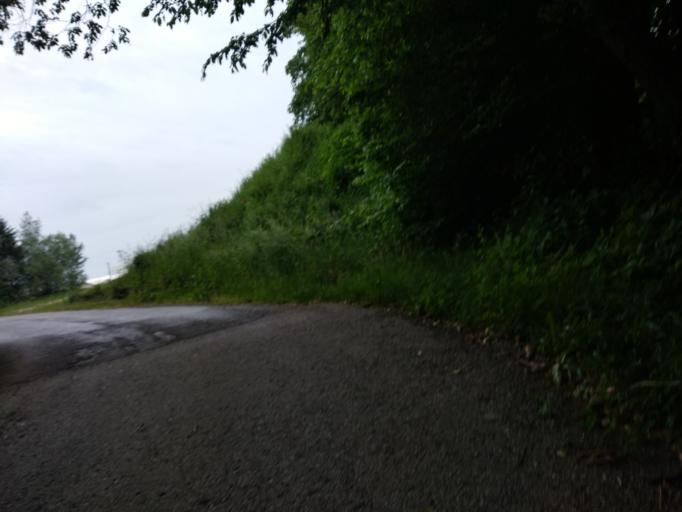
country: DE
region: Baden-Wuerttemberg
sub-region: Tuebingen Region
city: Aitrach
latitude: 47.9392
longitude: 10.0835
